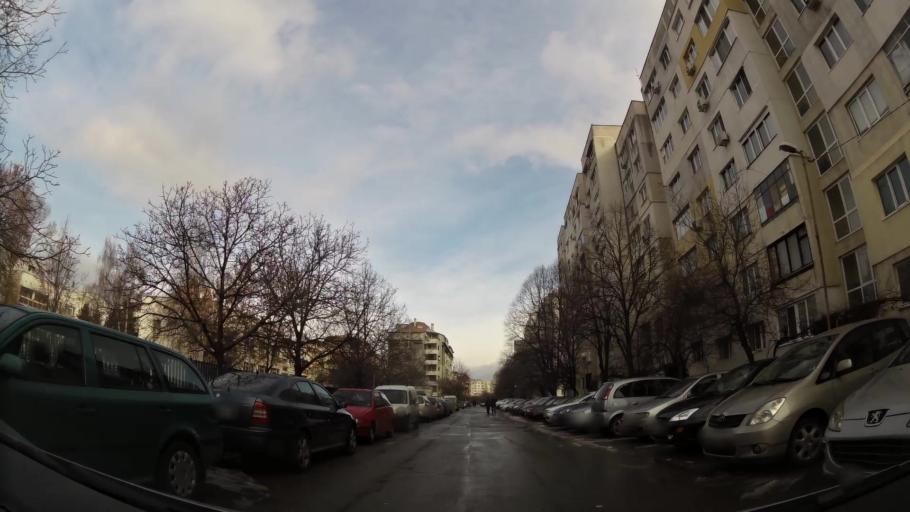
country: BG
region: Sofia-Capital
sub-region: Stolichna Obshtina
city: Sofia
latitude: 42.7140
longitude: 23.2700
